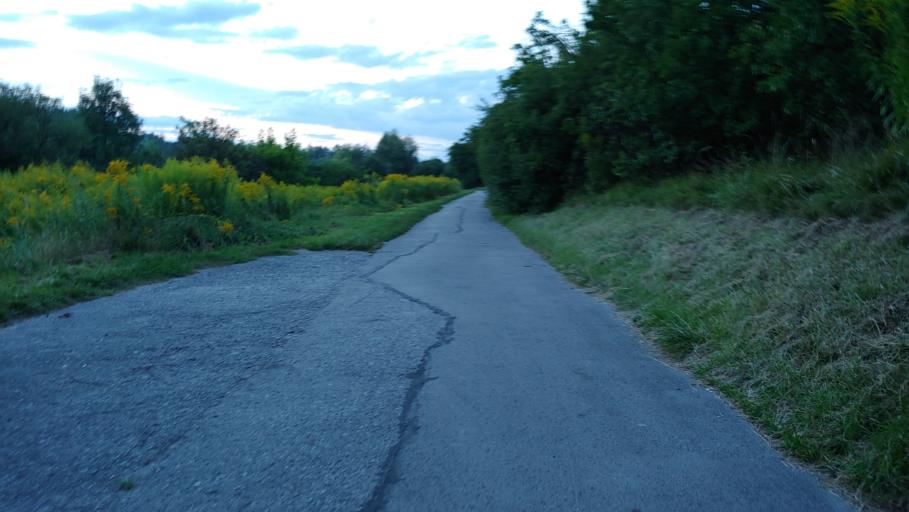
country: PL
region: Lesser Poland Voivodeship
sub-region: Powiat chrzanowski
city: Trzebinia
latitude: 50.1629
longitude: 19.4678
